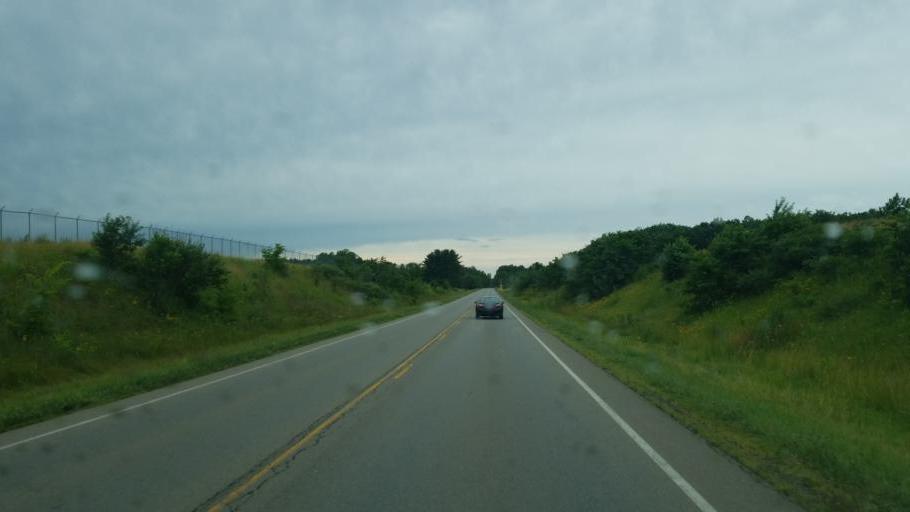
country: US
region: Ohio
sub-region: Richland County
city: Lincoln Heights
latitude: 40.8259
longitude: -82.5033
